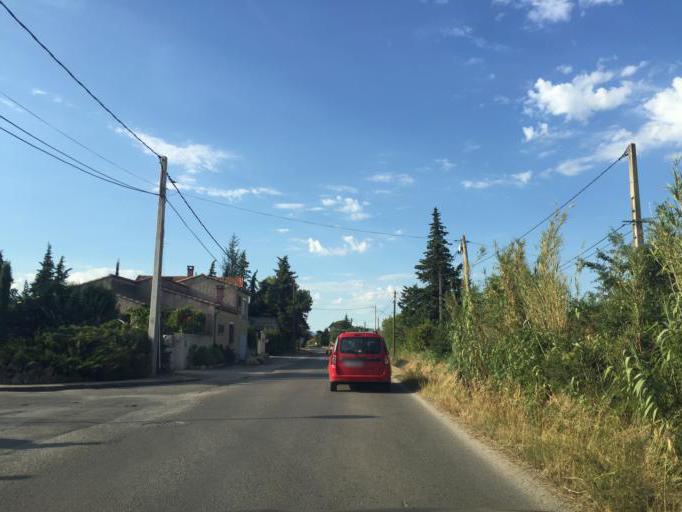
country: FR
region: Provence-Alpes-Cote d'Azur
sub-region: Departement du Vaucluse
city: Pernes-les-Fontaines
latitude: 44.0123
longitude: 5.0552
